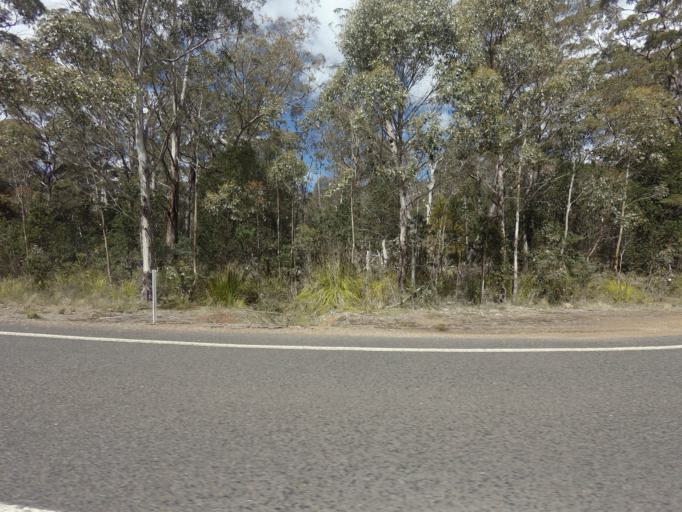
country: AU
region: Tasmania
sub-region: Northern Midlands
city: Evandale
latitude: -42.0038
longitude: 147.7233
